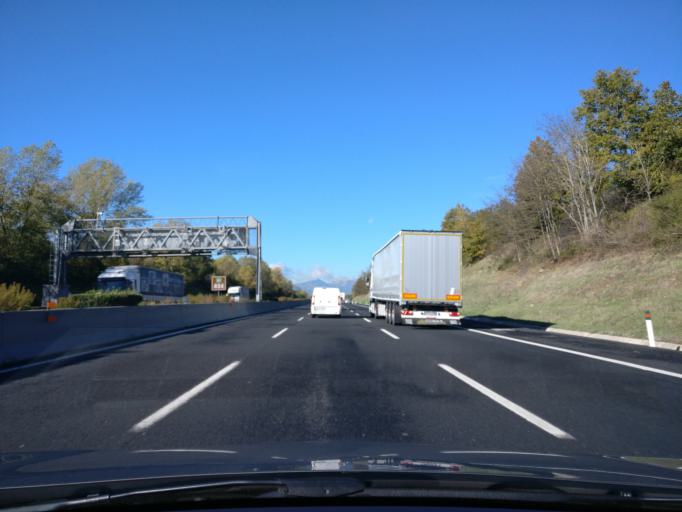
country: IT
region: Latium
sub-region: Provincia di Frosinone
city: Ceprano
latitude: 41.5469
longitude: 13.4761
